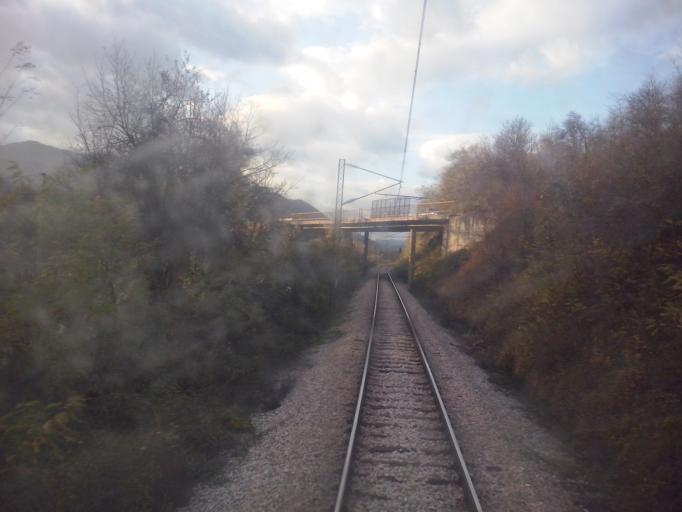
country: RS
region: Central Serbia
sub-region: Zlatiborski Okrug
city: Kosjeric
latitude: 43.9906
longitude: 19.9222
